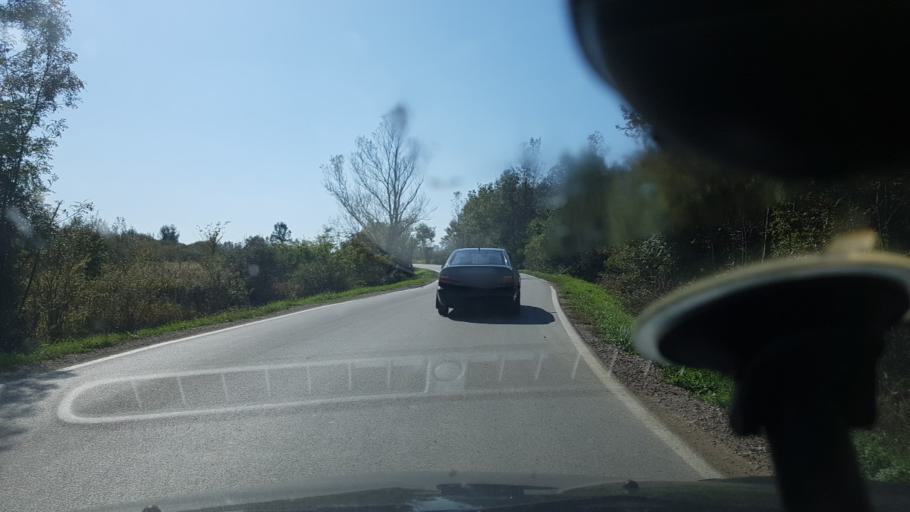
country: HR
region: Zagrebacka
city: Lupoglav
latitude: 45.7282
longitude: 16.3041
